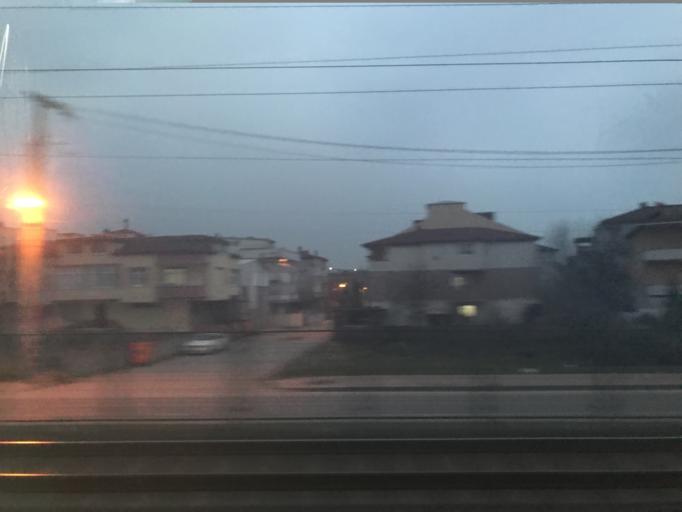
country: TR
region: Kocaeli
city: Darica
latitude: 40.7876
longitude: 29.3988
